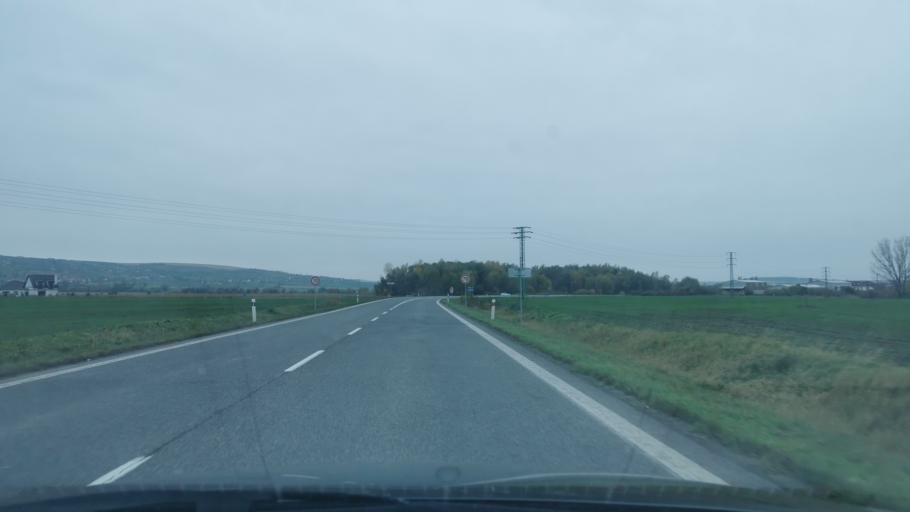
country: SK
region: Trnavsky
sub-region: Okres Skalica
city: Skalica
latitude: 48.8392
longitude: 17.2086
